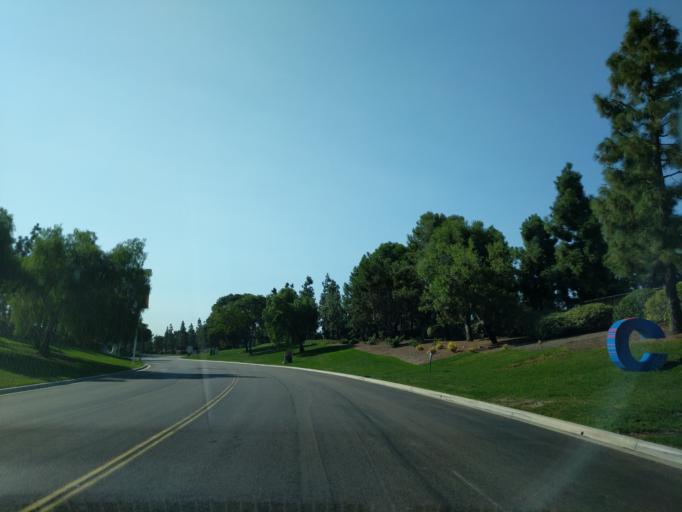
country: US
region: California
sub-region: San Diego County
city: Carlsbad
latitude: 33.1281
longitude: -117.3150
